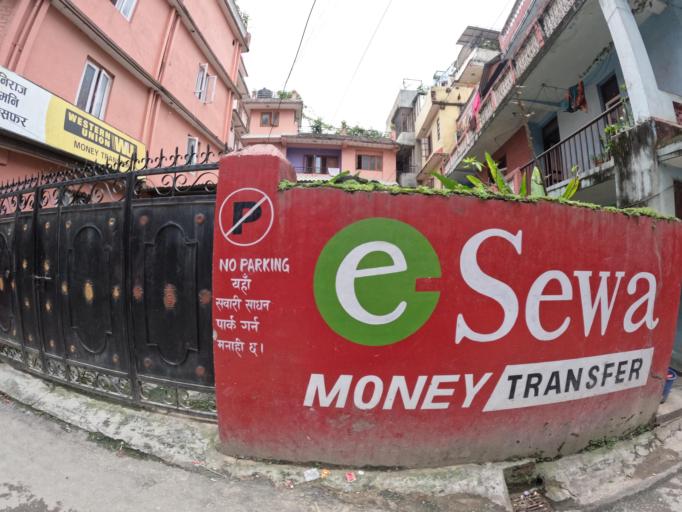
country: NP
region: Central Region
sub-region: Bagmati Zone
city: Kathmandu
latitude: 27.7372
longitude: 85.3115
